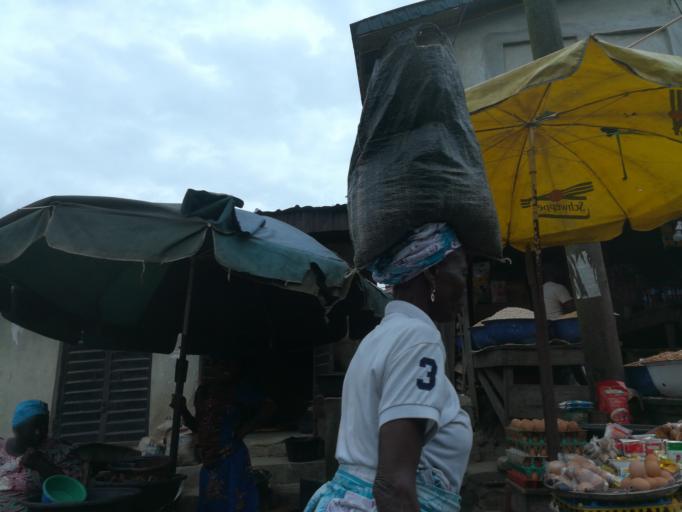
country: NG
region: Lagos
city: Ebute Metta
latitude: 6.4820
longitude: 3.3853
